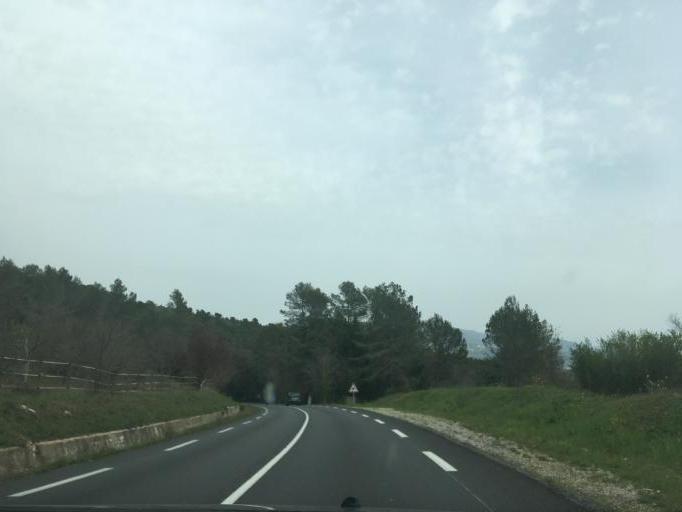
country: FR
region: Provence-Alpes-Cote d'Azur
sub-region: Departement du Var
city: Montauroux
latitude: 43.6069
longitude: 6.8093
